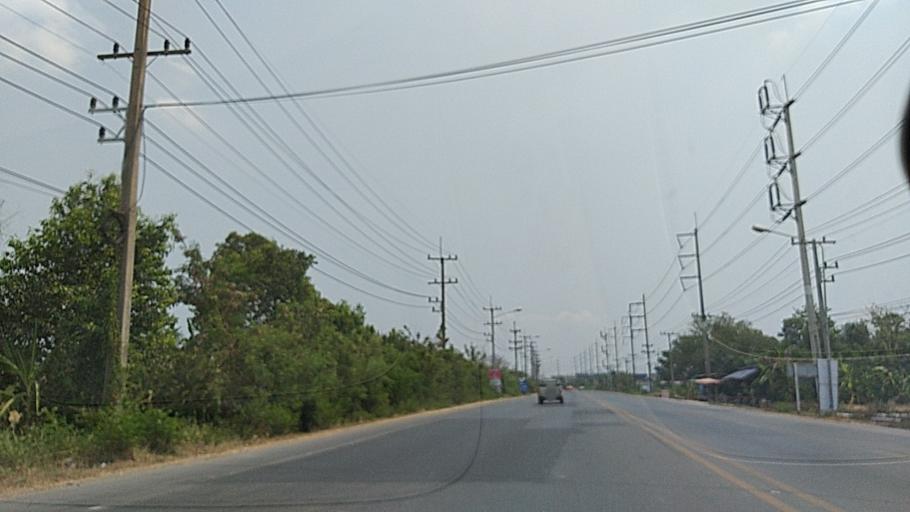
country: TH
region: Bangkok
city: Nong Chok
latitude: 13.9613
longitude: 100.8992
